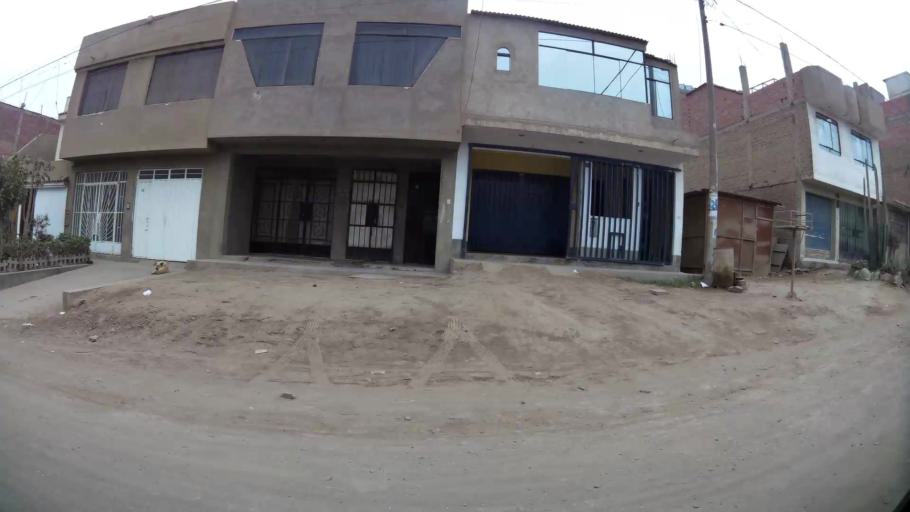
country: PE
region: Lima
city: Ventanilla
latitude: -11.9270
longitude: -77.0828
